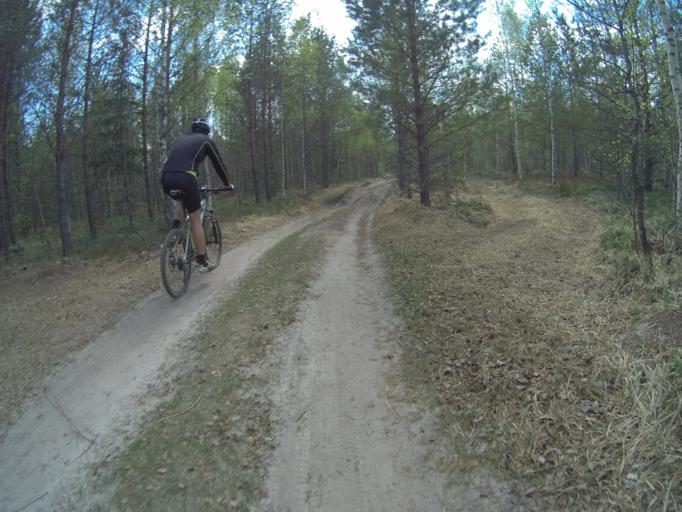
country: RU
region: Vladimir
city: Raduzhnyy
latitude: 55.9550
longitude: 40.2020
